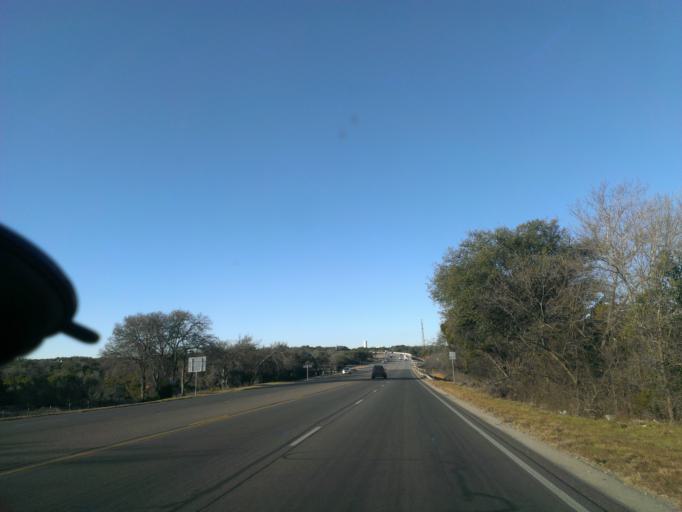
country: US
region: Texas
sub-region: Travis County
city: Bee Cave
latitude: 30.2206
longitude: -97.9581
